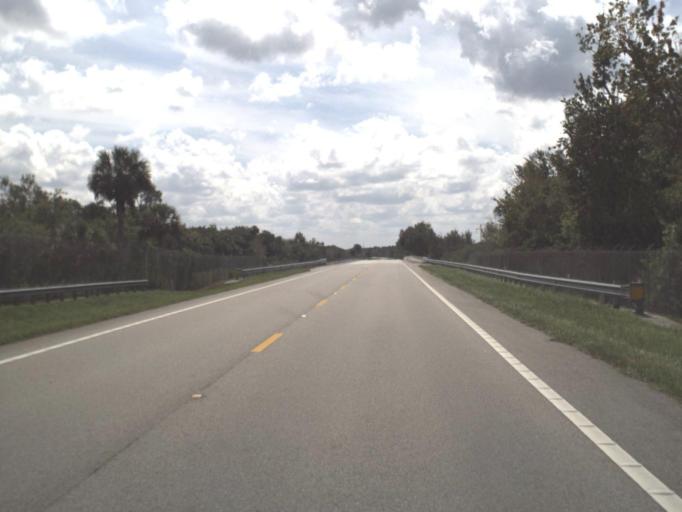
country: US
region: Florida
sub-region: Collier County
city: Immokalee
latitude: 26.2154
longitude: -81.3453
